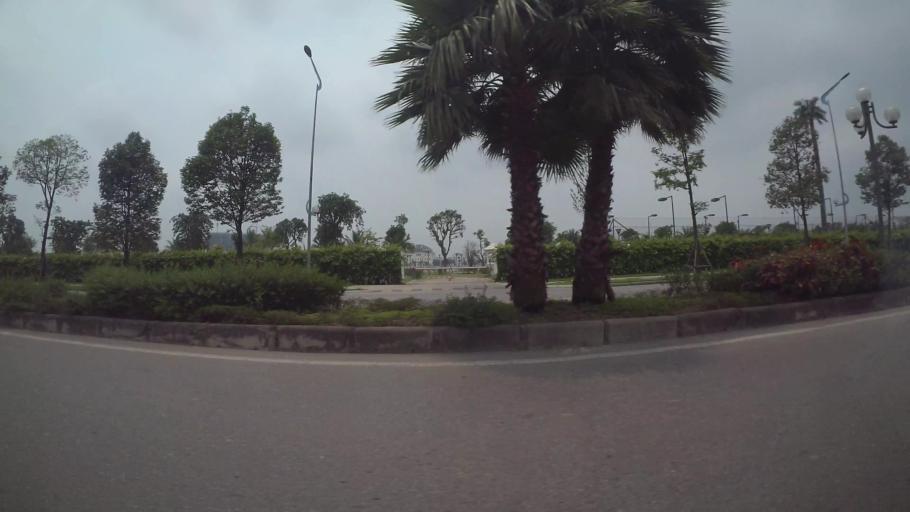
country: VN
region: Ha Noi
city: Trau Quy
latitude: 21.0490
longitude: 105.9090
